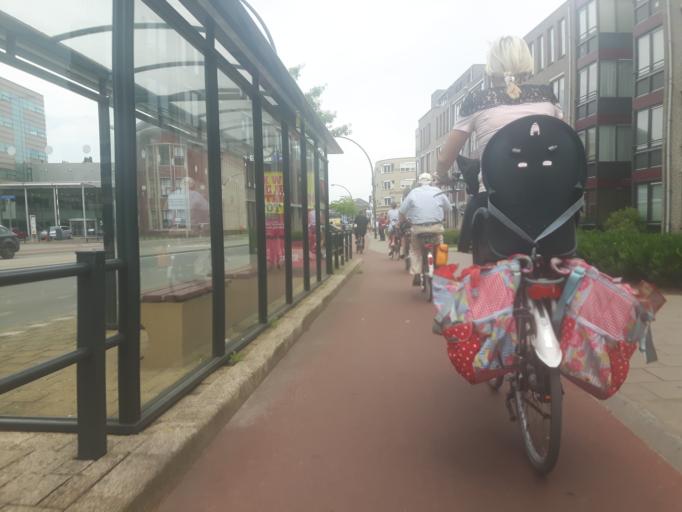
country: NL
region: Overijssel
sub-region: Gemeente Hengelo
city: Hengelo
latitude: 52.2675
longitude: 6.7921
